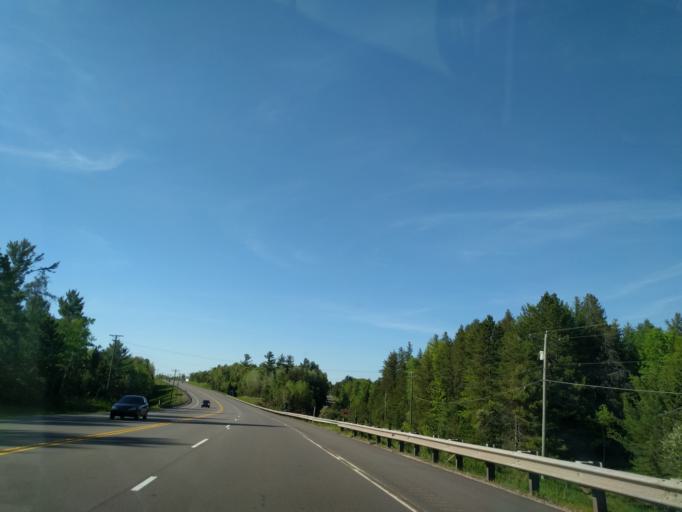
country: US
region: Michigan
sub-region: Marquette County
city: K. I. Sawyer Air Force Base
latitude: 46.4138
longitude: -87.4069
